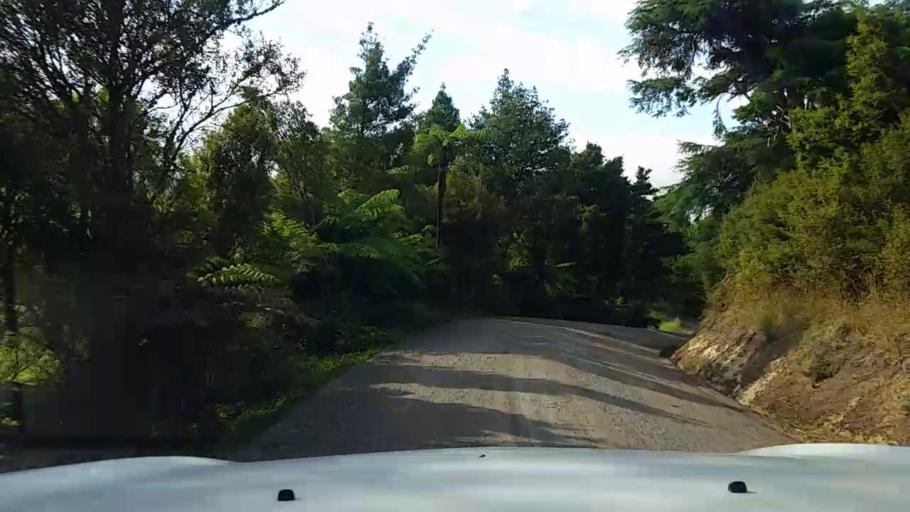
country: NZ
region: Northland
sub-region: Whangarei
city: Maungatapere
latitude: -35.6760
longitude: 174.1769
